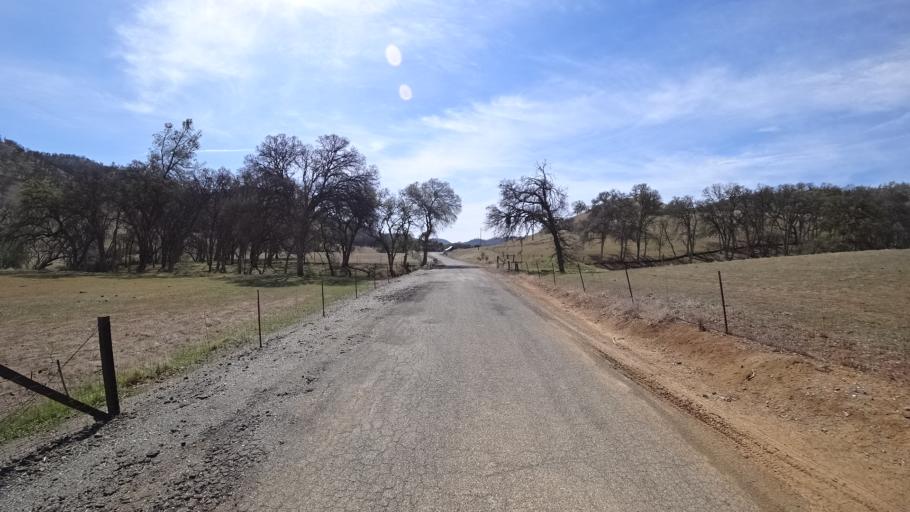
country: US
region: California
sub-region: Glenn County
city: Willows
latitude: 39.4892
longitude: -122.4530
